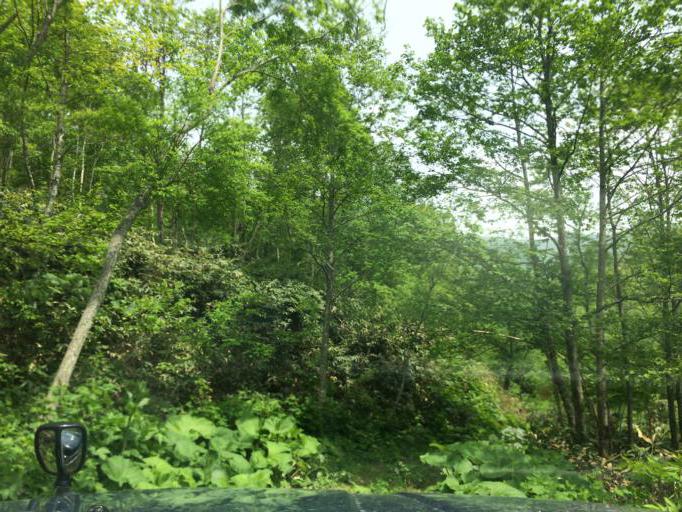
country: JP
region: Hokkaido
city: Niseko Town
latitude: 42.6884
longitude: 140.6221
